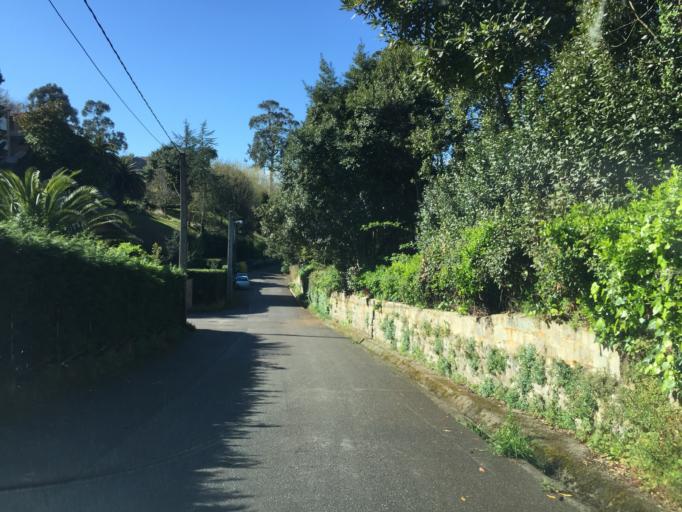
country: ES
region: Asturias
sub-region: Province of Asturias
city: Gijon
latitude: 43.5436
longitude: -5.6224
